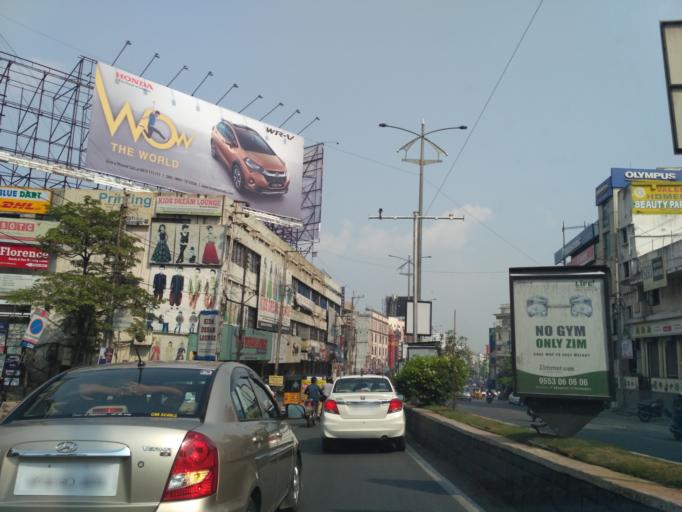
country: IN
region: Telangana
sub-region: Hyderabad
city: Hyderabad
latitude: 17.4060
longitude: 78.4791
